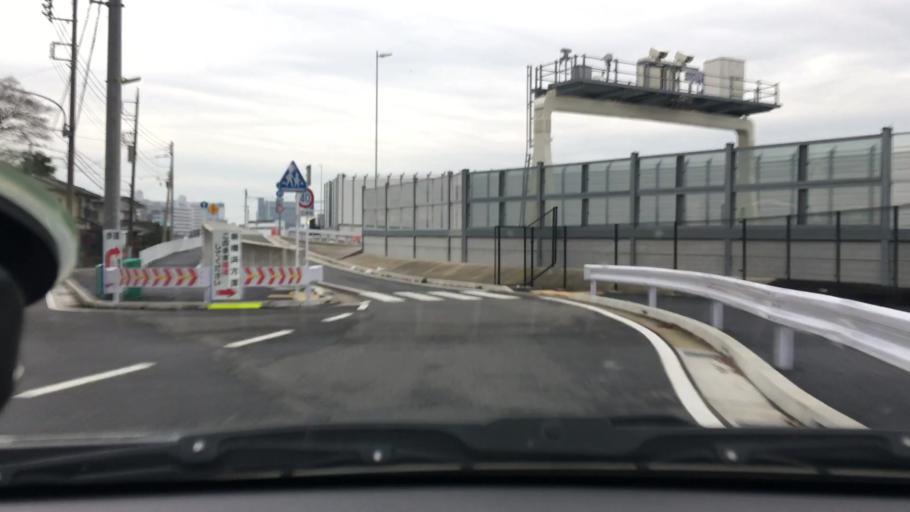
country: JP
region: Kanagawa
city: Yokohama
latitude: 35.5168
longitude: 139.6068
